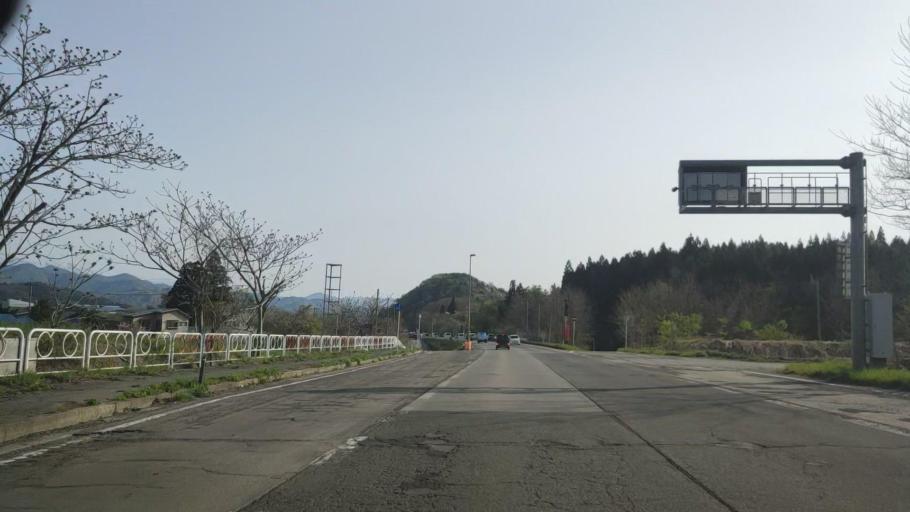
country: JP
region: Aomori
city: Aomori Shi
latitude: 40.8555
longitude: 140.8399
